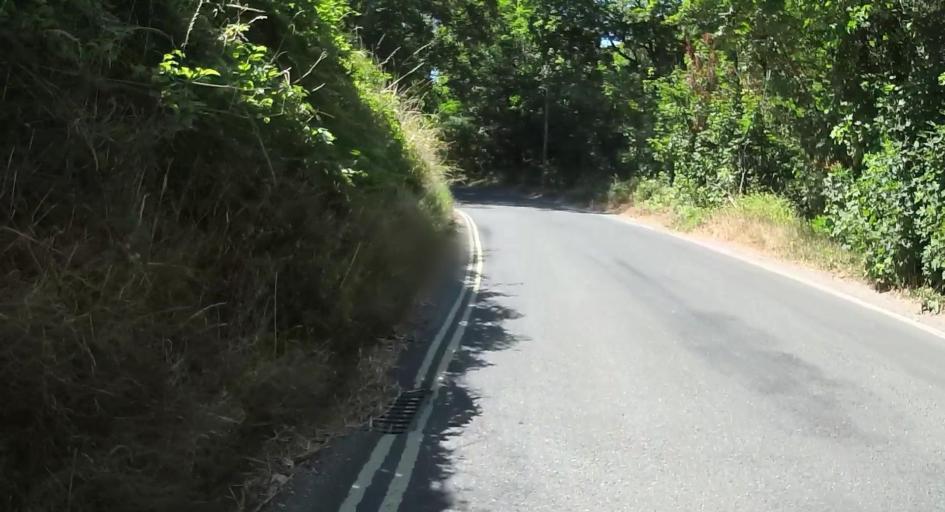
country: GB
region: England
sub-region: Dorset
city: Wareham
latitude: 50.6406
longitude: -2.0611
